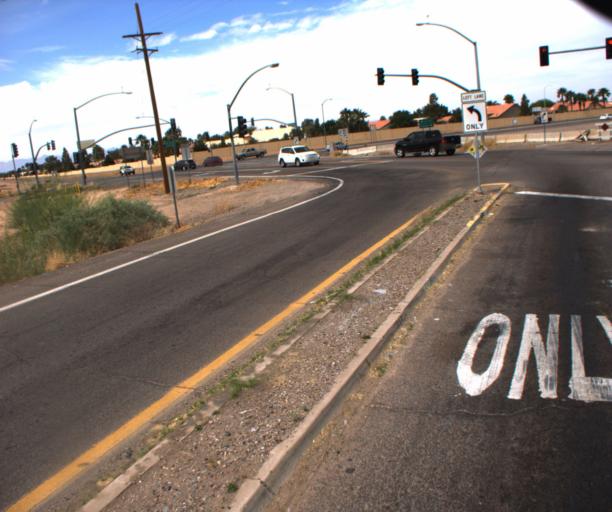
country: US
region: Arizona
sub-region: Maricopa County
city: Sun Lakes
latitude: 33.2038
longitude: -111.8400
